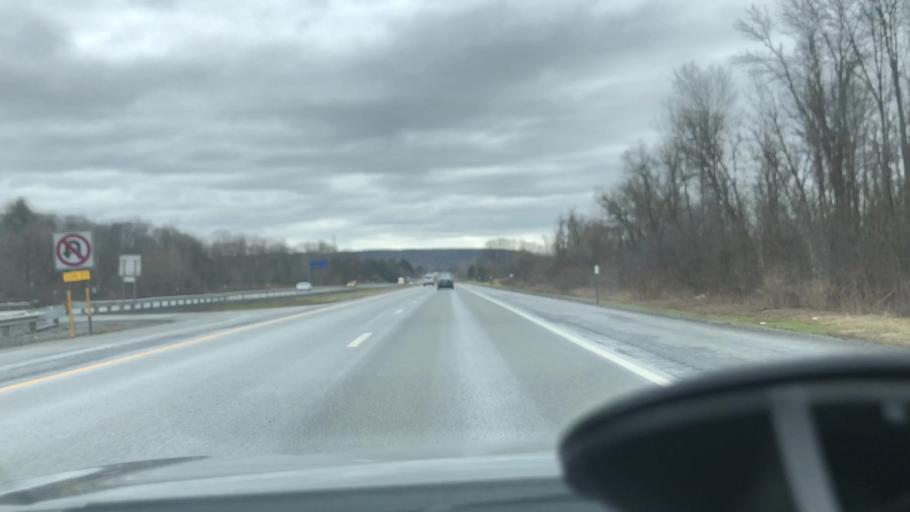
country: US
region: New York
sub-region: Herkimer County
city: Frankfort
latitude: 43.0721
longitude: -75.0965
